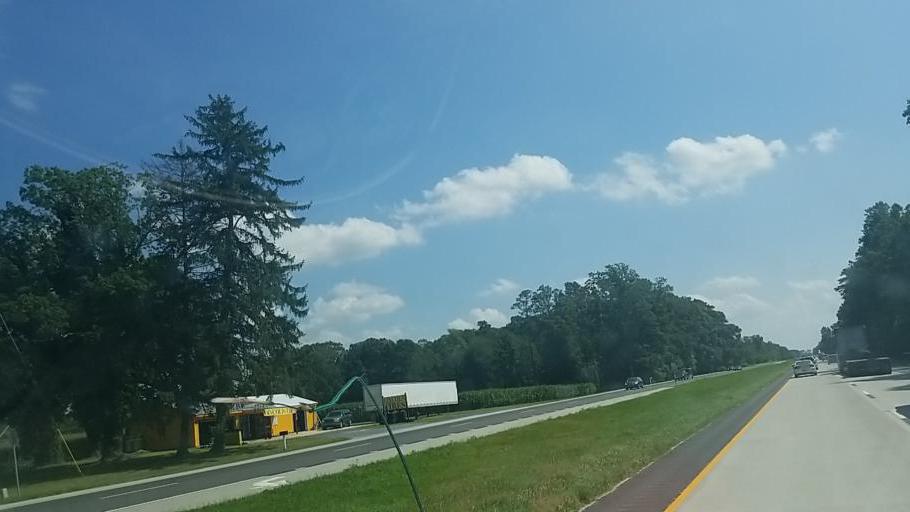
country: US
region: Delaware
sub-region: Sussex County
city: Milford
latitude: 38.8474
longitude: -75.4393
